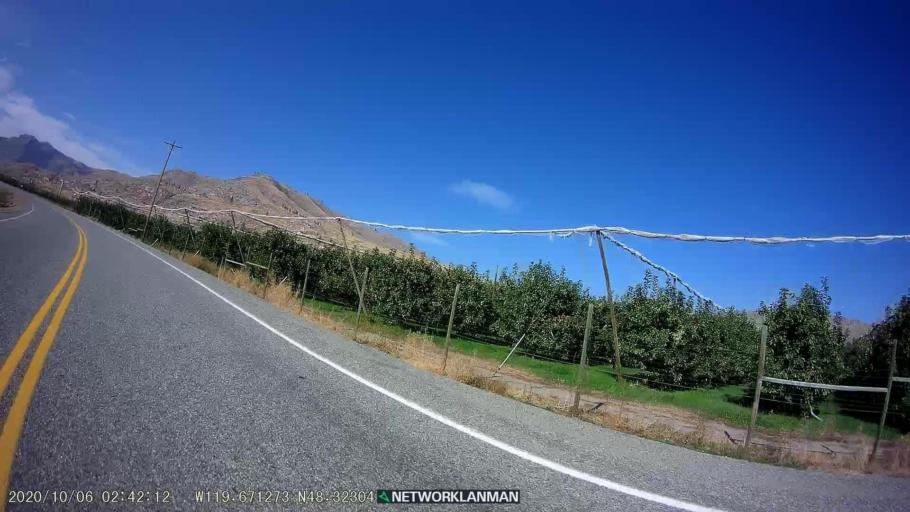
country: US
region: Washington
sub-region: Okanogan County
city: Okanogan
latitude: 48.3231
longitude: -119.6713
